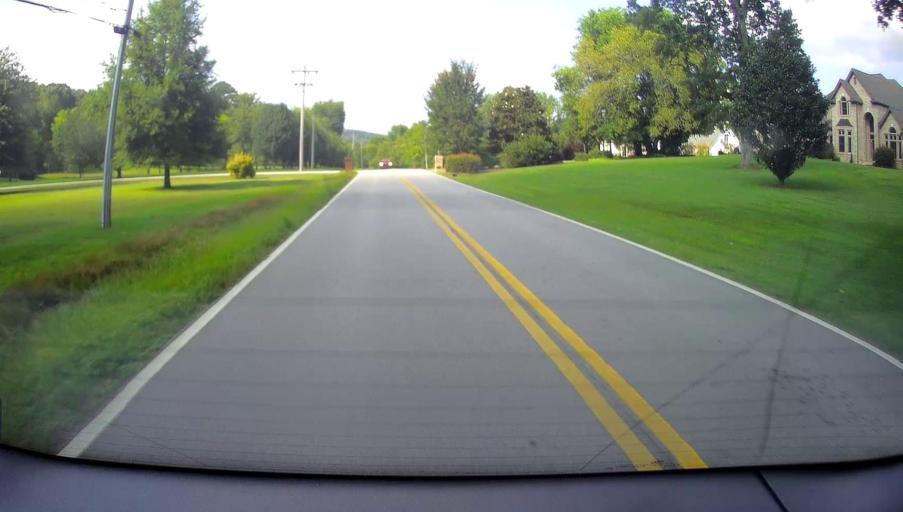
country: US
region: Georgia
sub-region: Catoosa County
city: Ringgold
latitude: 34.9249
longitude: -85.0848
